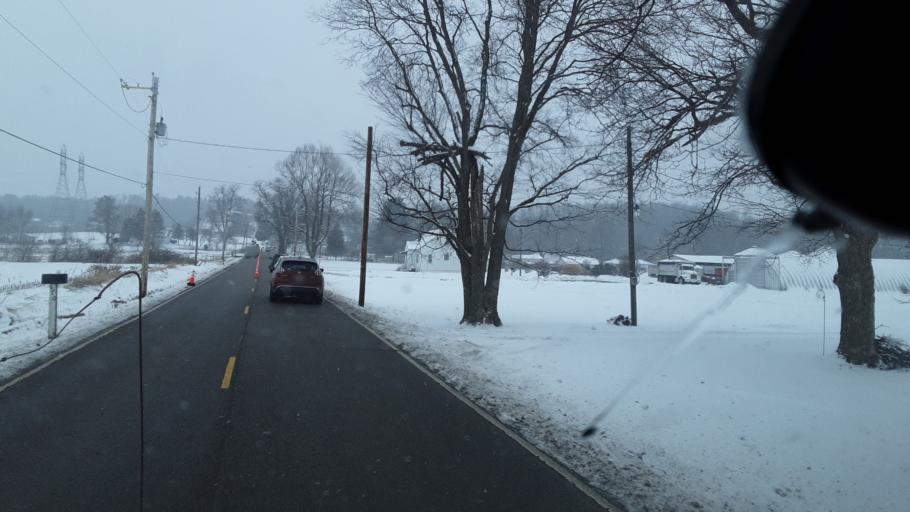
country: US
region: Ohio
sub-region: Licking County
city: Heath
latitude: 40.0337
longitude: -82.4796
